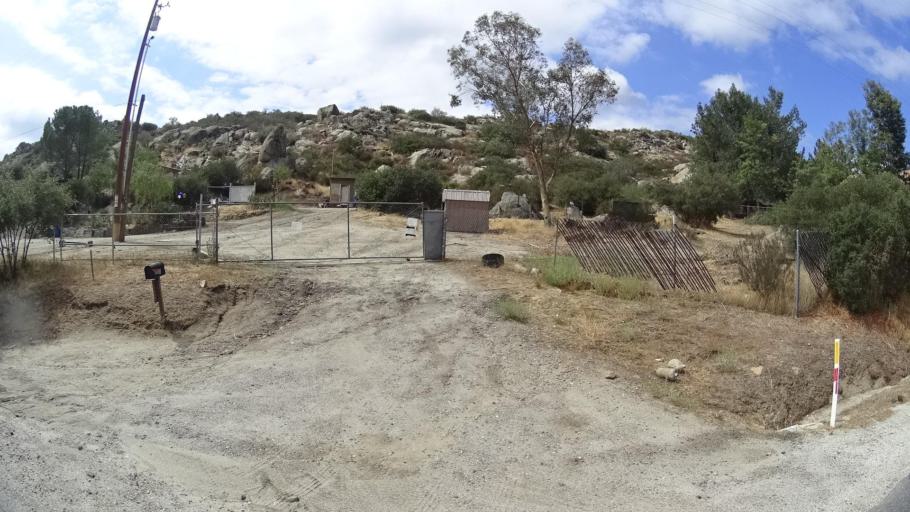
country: US
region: California
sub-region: San Diego County
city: Campo
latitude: 32.6809
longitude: -116.4889
